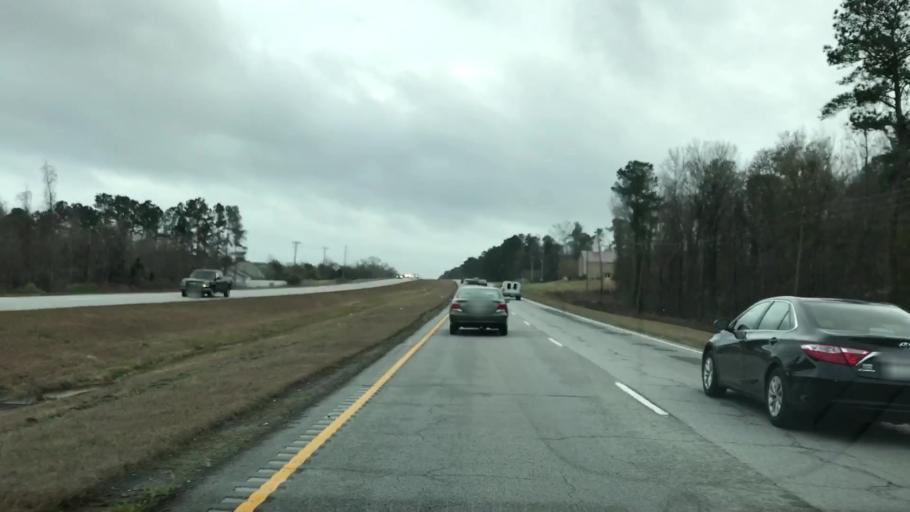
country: US
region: South Carolina
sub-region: Berkeley County
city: Moncks Corner
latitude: 33.1389
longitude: -80.0323
